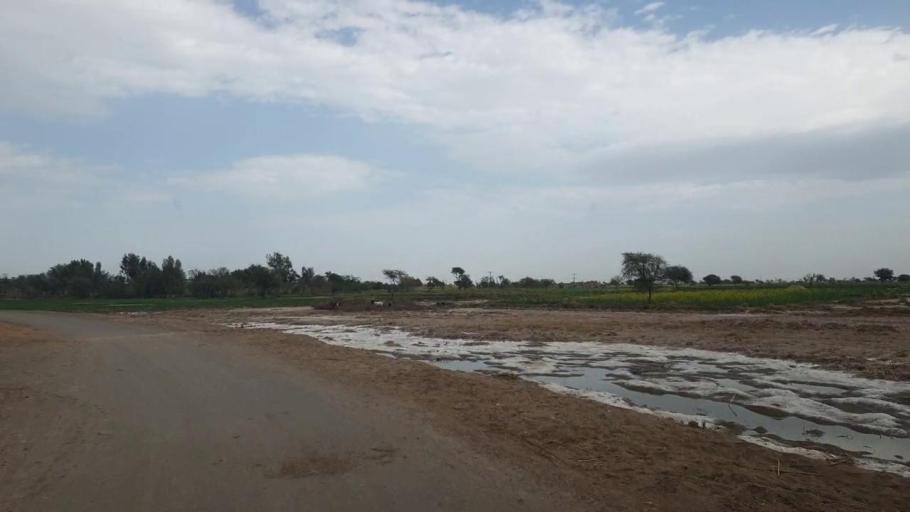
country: PK
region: Sindh
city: Hala
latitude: 25.9813
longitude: 68.4219
